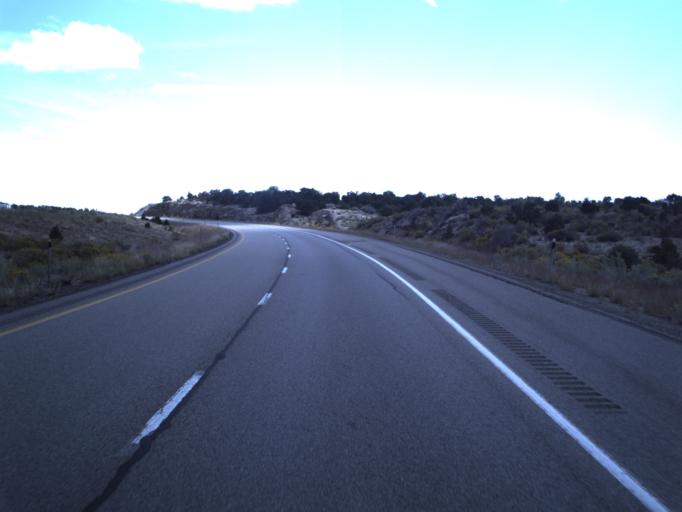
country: US
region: Utah
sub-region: Emery County
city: Ferron
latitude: 38.8611
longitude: -110.8417
